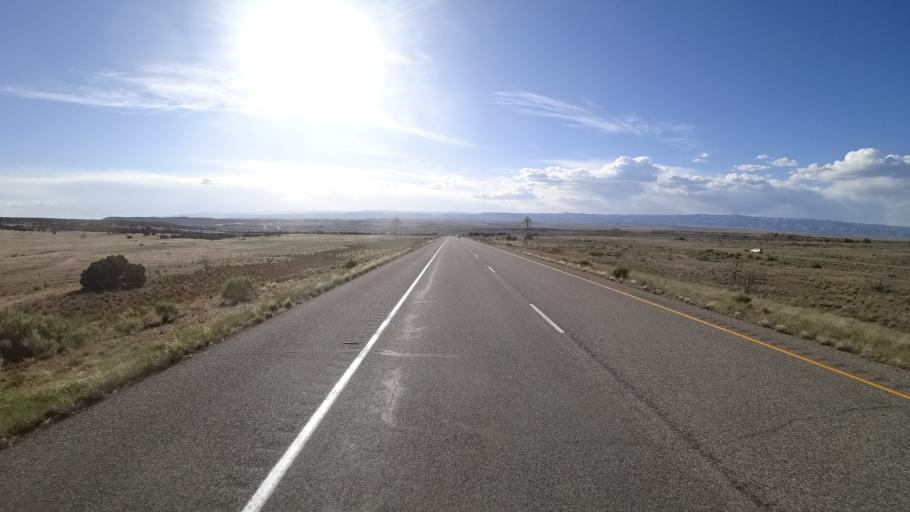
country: US
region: Colorado
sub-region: Mesa County
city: Loma
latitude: 39.1905
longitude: -109.0437
